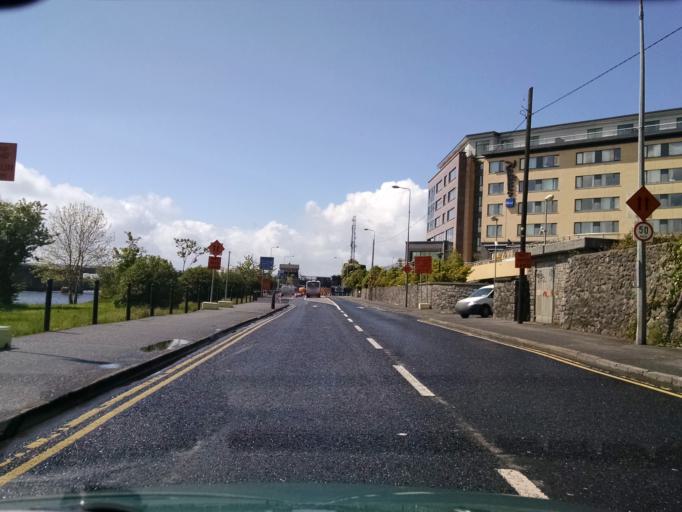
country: IE
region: Connaught
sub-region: County Galway
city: Gaillimh
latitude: 53.2746
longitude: -9.0418
